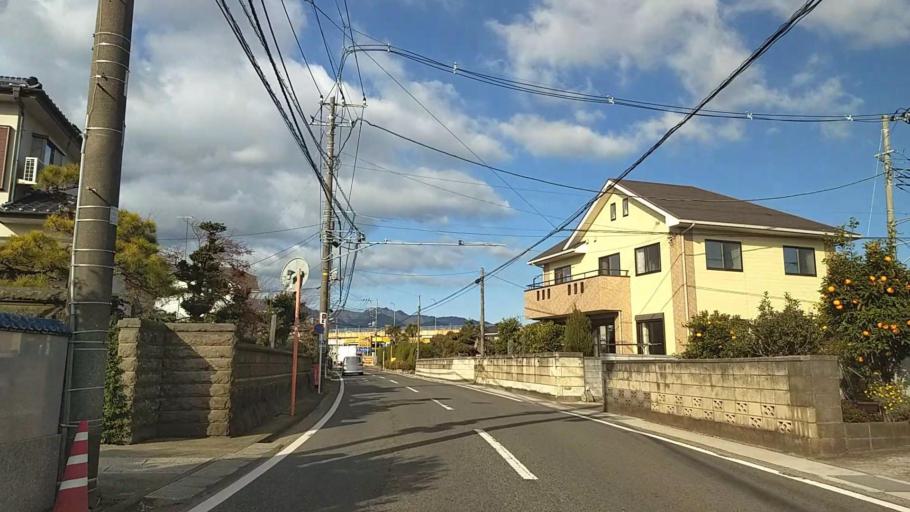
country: JP
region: Kanagawa
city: Atsugi
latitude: 35.4178
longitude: 139.3549
